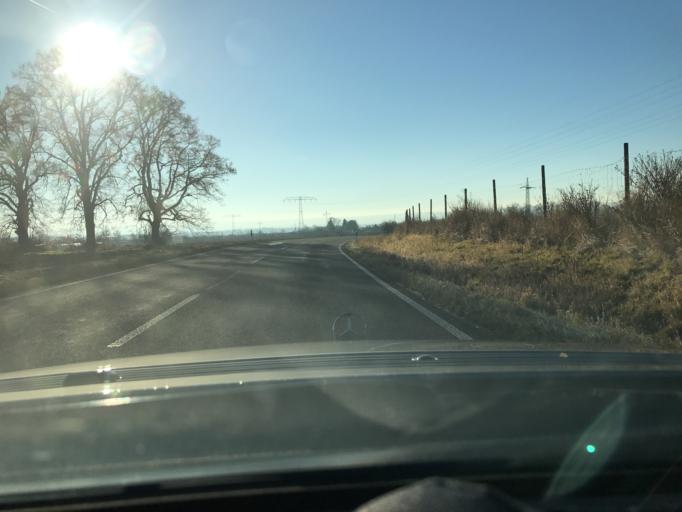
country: DE
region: Thuringia
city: Muehlhausen
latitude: 51.2352
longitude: 10.4838
